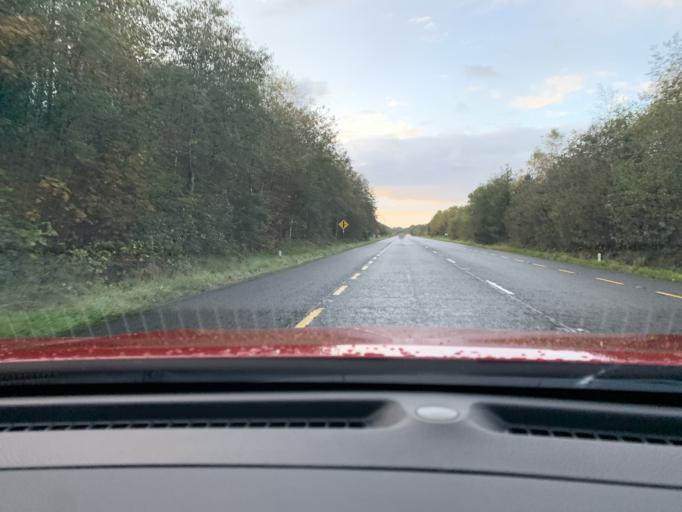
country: IE
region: Connaught
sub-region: County Leitrim
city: Carrick-on-Shannon
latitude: 53.9530
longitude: -8.1543
